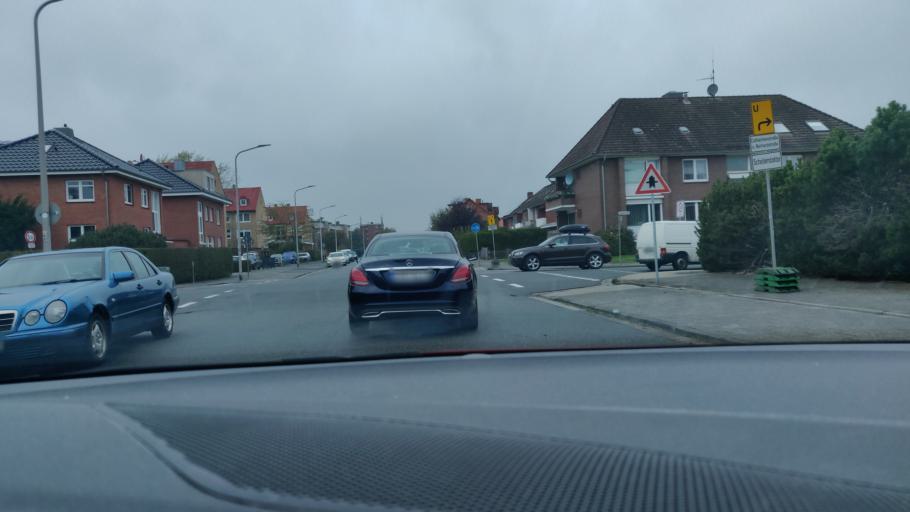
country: DE
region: Lower Saxony
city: Cuxhaven
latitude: 53.8687
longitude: 8.6904
